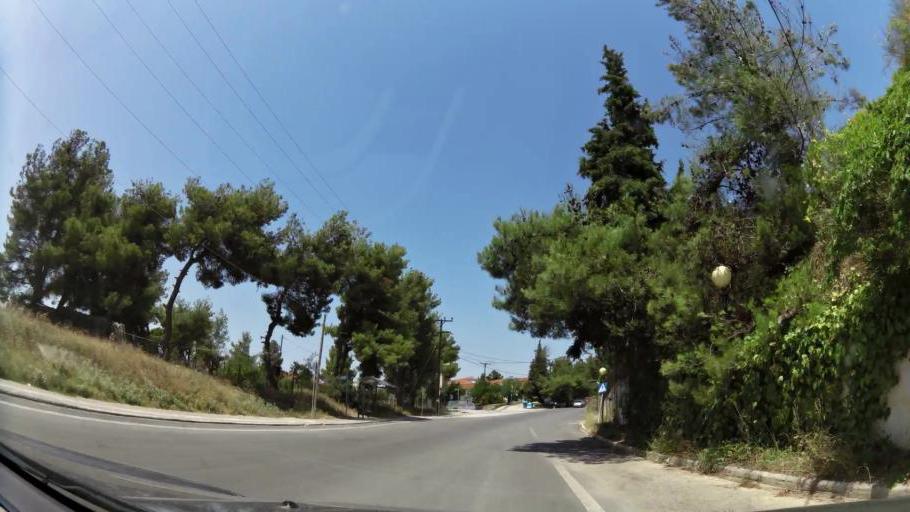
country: GR
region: Central Macedonia
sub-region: Nomos Thessalonikis
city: Trilofos
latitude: 40.4720
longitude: 22.9696
